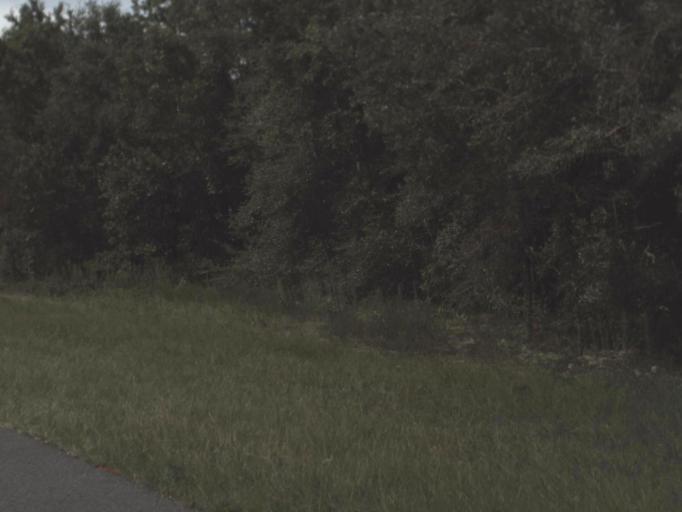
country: US
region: Florida
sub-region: Citrus County
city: Citrus Springs
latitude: 29.0035
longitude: -82.4472
